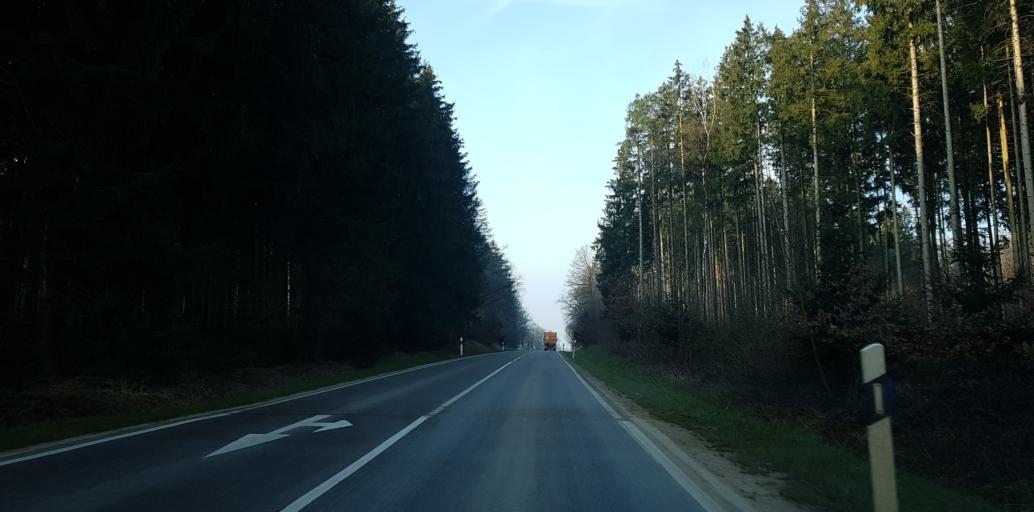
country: DE
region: Baden-Wuerttemberg
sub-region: Tuebingen Region
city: Erbach
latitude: 48.3488
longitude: 9.8519
